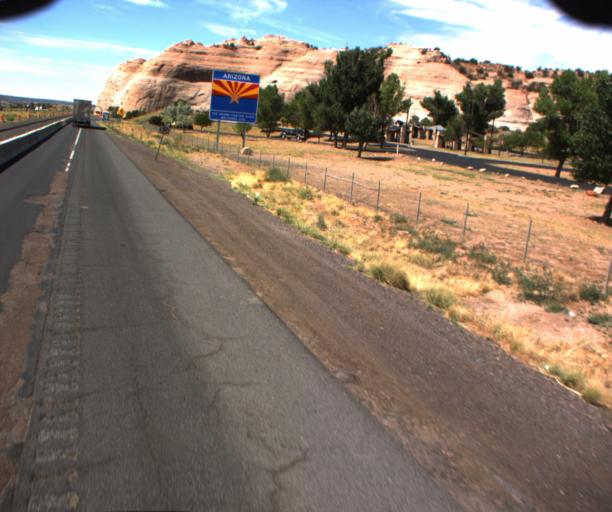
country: US
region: Arizona
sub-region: Apache County
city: Houck
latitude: 35.3528
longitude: -109.0570
